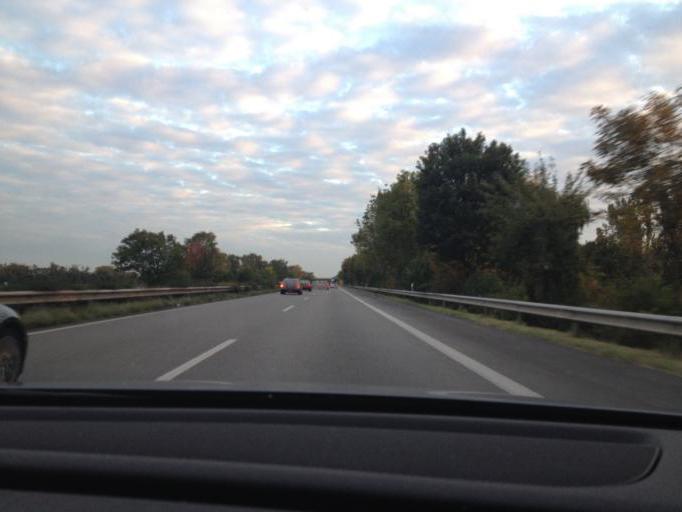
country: DE
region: Rheinland-Pfalz
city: Neuhofen
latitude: 49.4180
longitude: 8.4096
